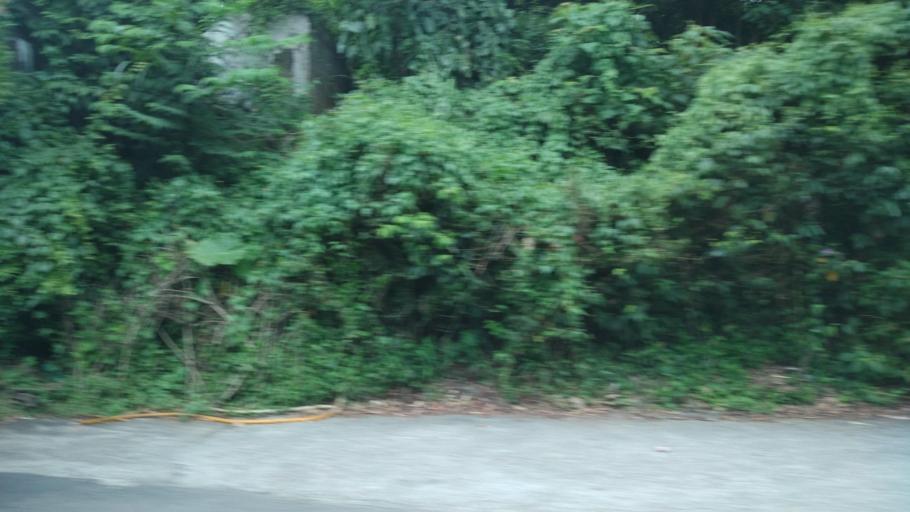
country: TW
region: Taipei
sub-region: Taipei
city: Banqiao
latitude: 24.9468
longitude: 121.4797
